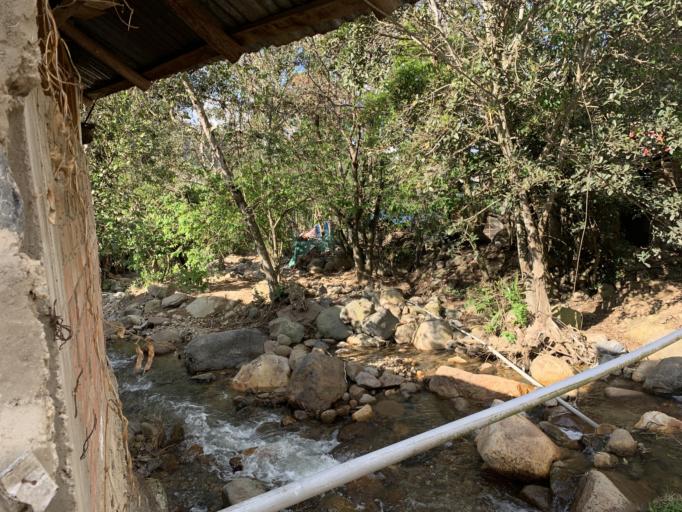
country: PE
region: Cajamarca
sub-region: Provincia de Chota
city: Querocoto
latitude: -6.3515
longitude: -79.1120
